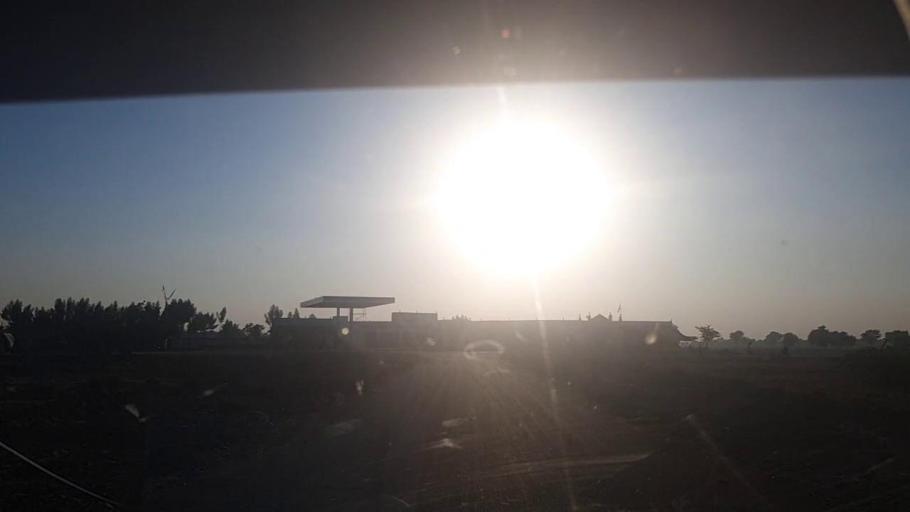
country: PK
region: Sindh
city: Hingorja
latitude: 27.2190
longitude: 68.4034
